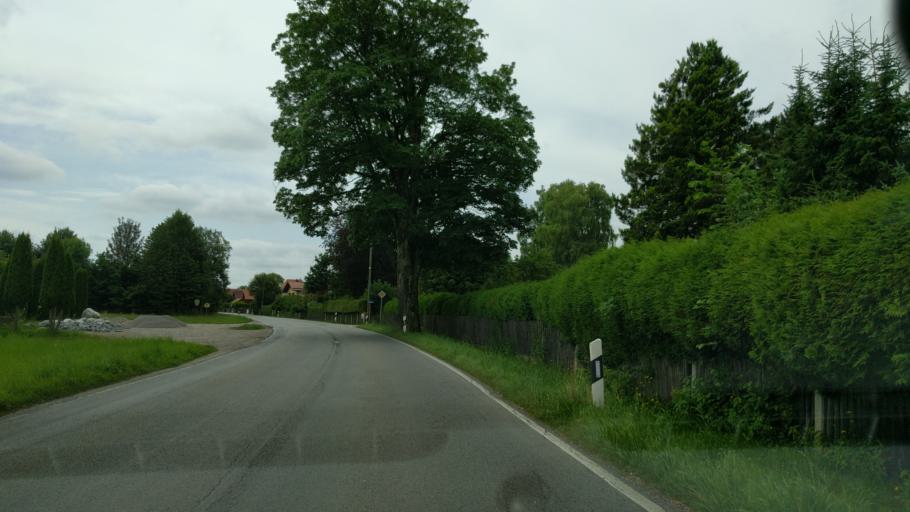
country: DE
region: Bavaria
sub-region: Upper Bavaria
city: Strasslach-Dingharting
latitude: 48.0090
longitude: 11.5146
